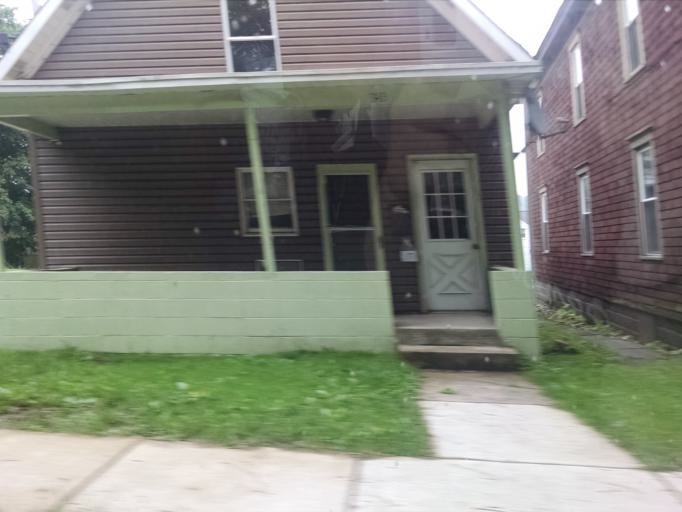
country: US
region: Pennsylvania
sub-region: Indiana County
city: Indiana
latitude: 40.6187
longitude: -79.1509
